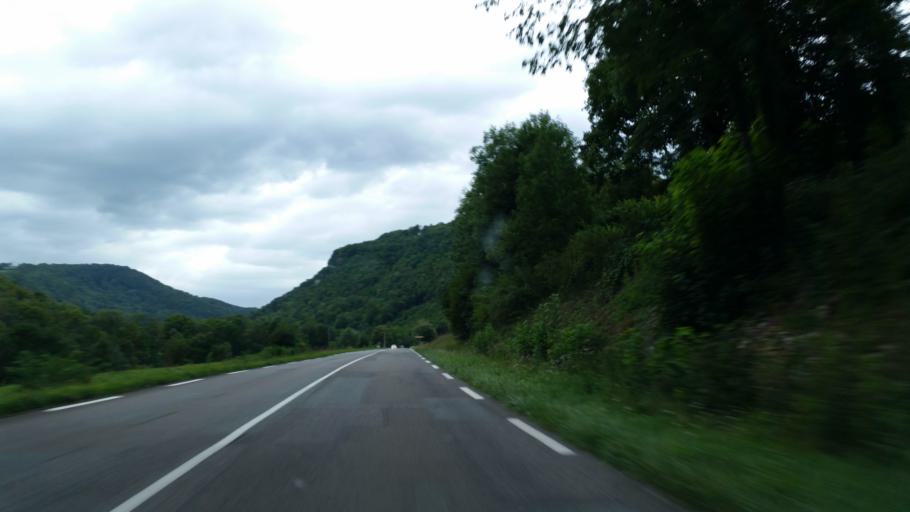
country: FR
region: Franche-Comte
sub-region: Departement du Doubs
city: Saint-Hippolyte
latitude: 47.3239
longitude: 6.7890
